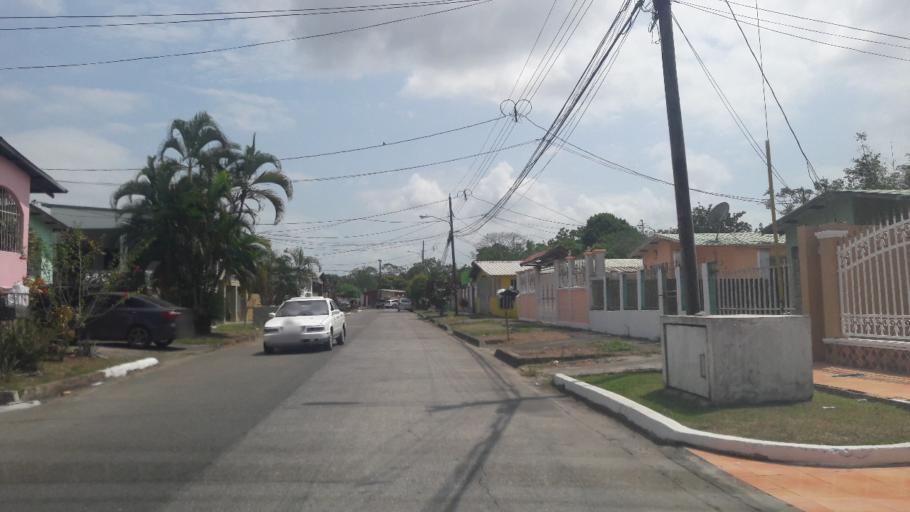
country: PA
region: Panama
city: Alcalde Diaz
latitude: 9.1377
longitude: -79.5516
